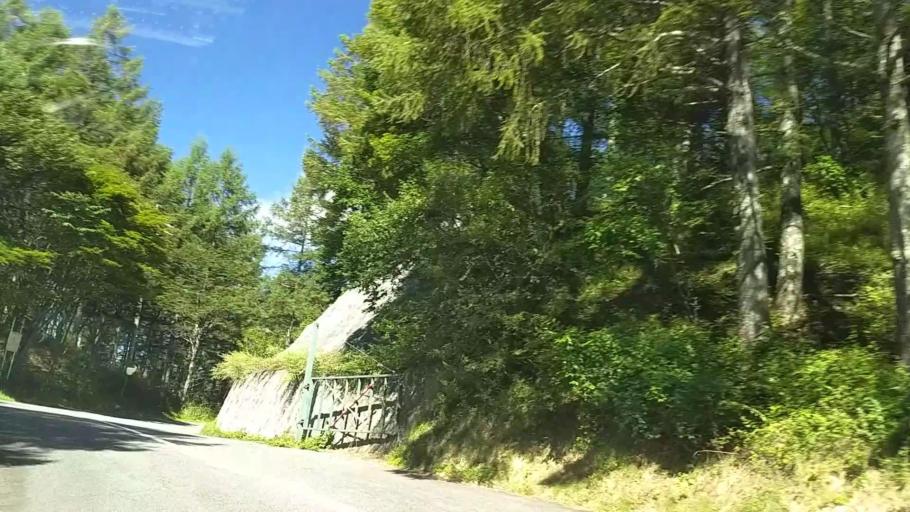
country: JP
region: Nagano
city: Matsumoto
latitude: 36.2029
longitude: 138.1055
